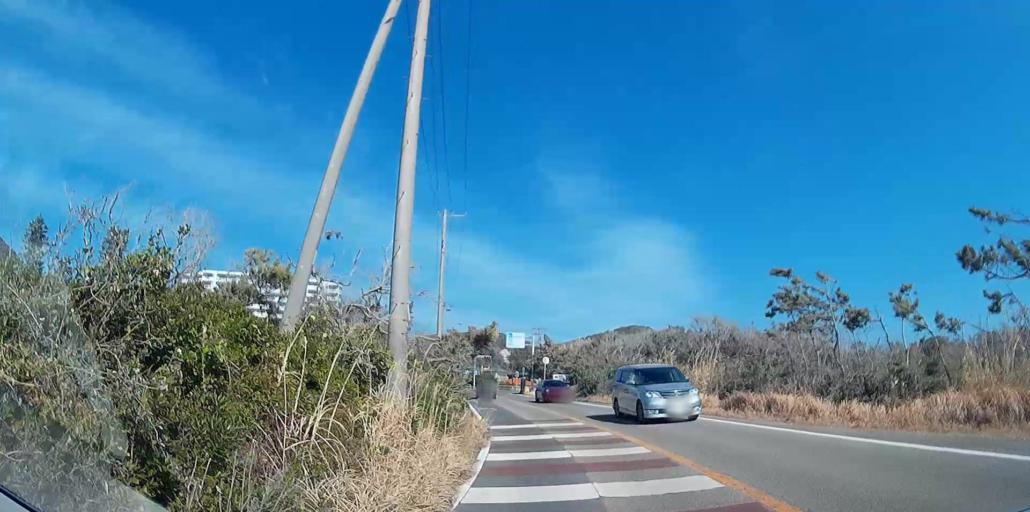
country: JP
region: Chiba
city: Tateyama
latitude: 34.9076
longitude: 139.8678
